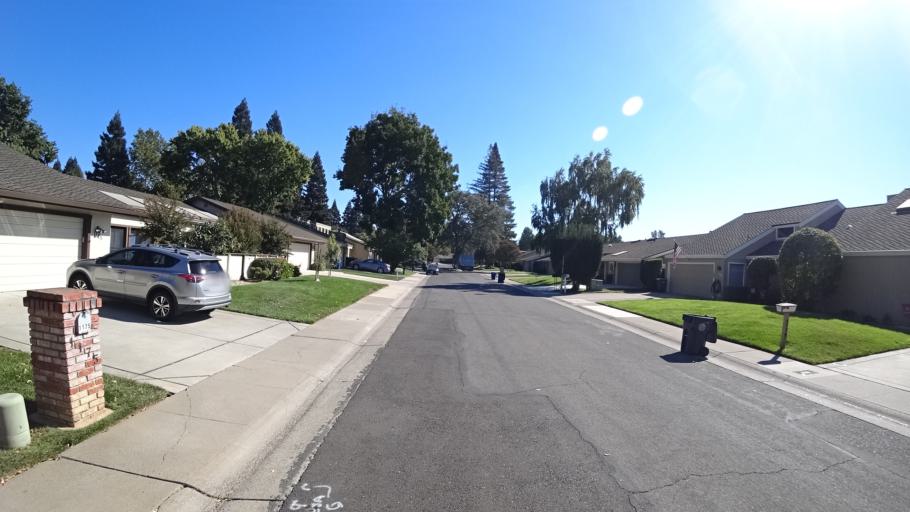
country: US
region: California
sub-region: Sacramento County
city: Parkway
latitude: 38.4858
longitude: -121.5153
